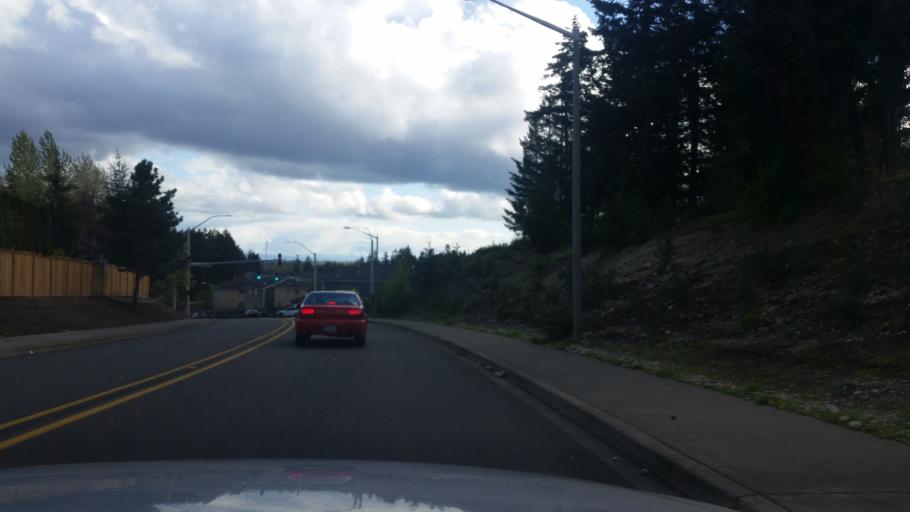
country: US
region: Washington
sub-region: Pierce County
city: Graham
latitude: 47.0896
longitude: -122.3115
